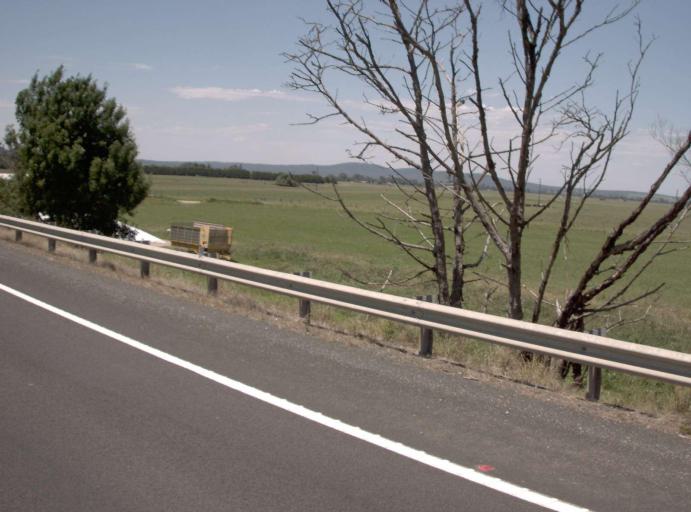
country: AU
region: Victoria
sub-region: East Gippsland
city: Lakes Entrance
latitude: -37.7246
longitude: 148.4488
